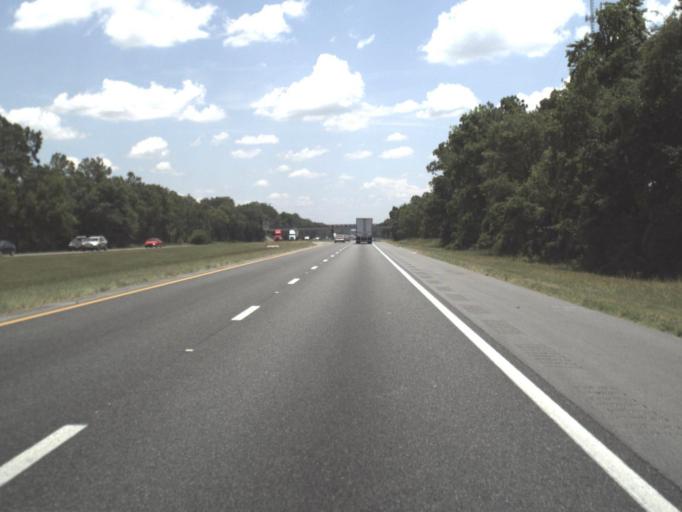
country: US
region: Florida
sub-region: Madison County
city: Madison
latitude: 30.3626
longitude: -83.2219
